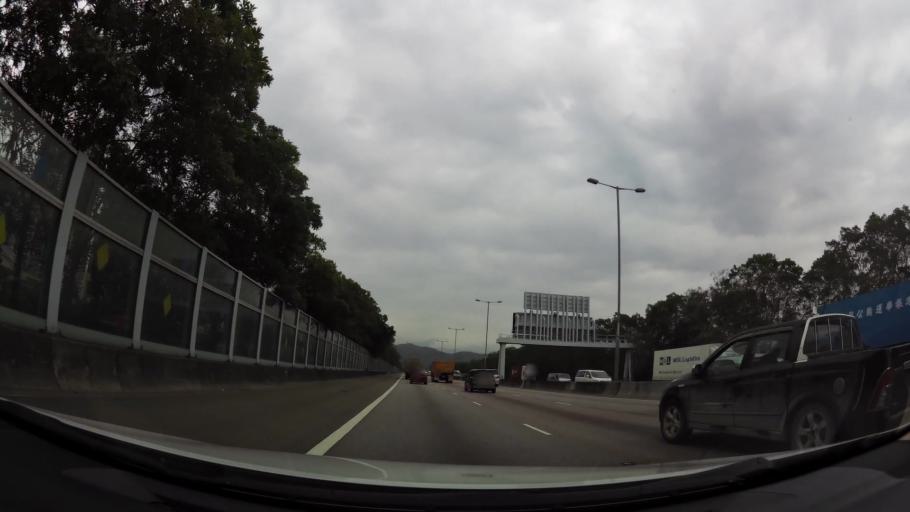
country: HK
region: Yuen Long
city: Yuen Long Kau Hui
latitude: 22.4354
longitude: 114.0227
